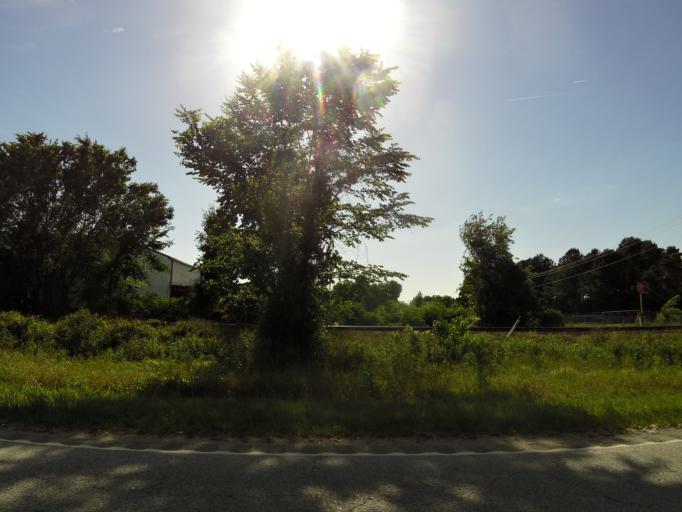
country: US
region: South Carolina
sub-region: Allendale County
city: Fairfax
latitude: 32.9382
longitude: -81.2370
